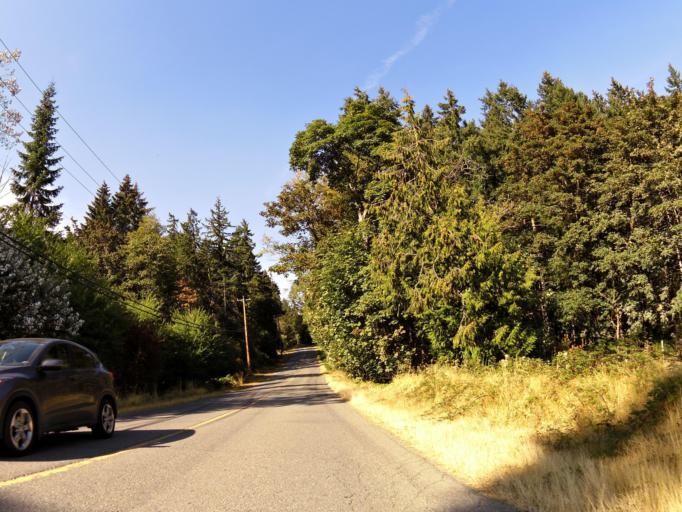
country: CA
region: British Columbia
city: North Saanich
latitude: 48.6809
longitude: -123.5507
